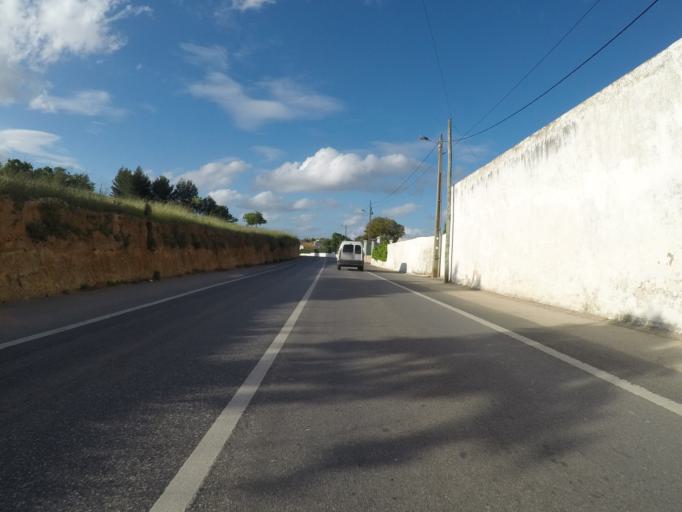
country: PT
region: Faro
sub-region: Lagoa
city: Carvoeiro
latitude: 37.1124
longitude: -8.4554
